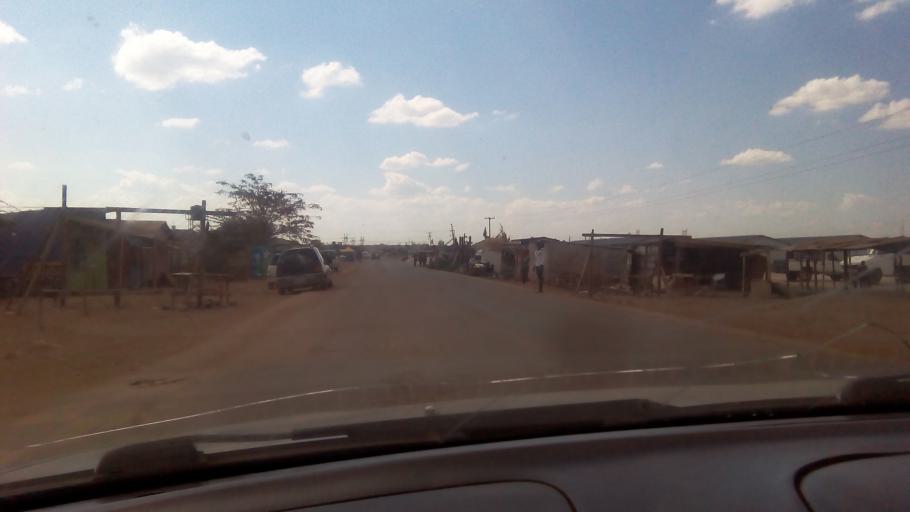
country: ZM
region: Lusaka
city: Lusaka
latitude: -15.4673
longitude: 28.3421
